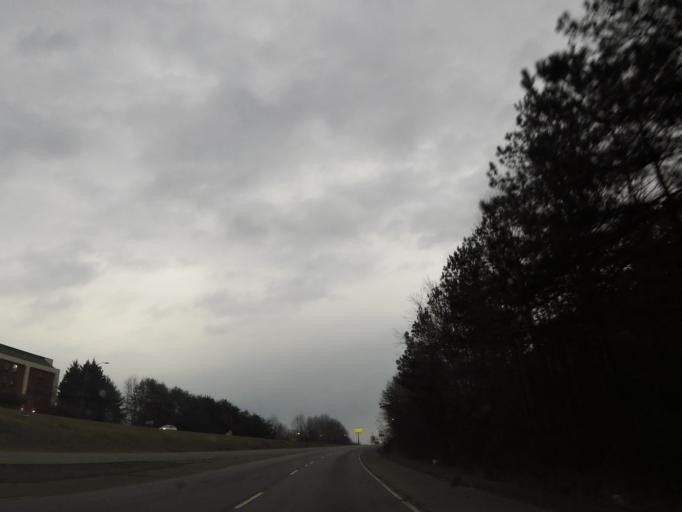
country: US
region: South Carolina
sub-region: Greenville County
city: Travelers Rest
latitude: 34.9563
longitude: -82.4384
